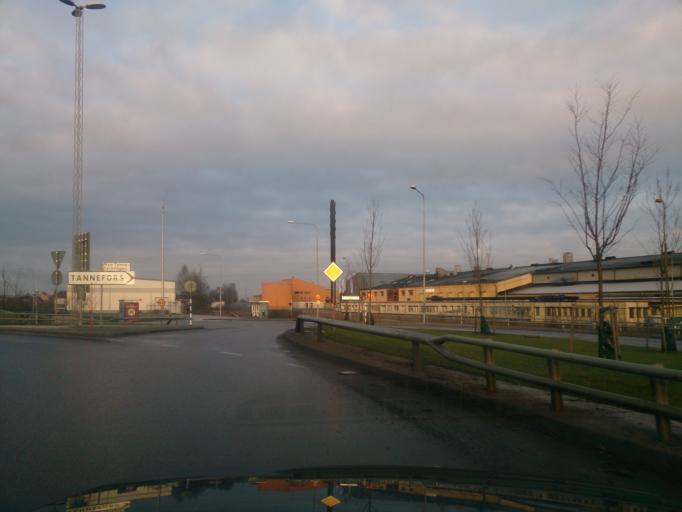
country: SE
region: OEstergoetland
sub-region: Linkopings Kommun
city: Linkoping
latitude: 58.4014
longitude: 15.6535
